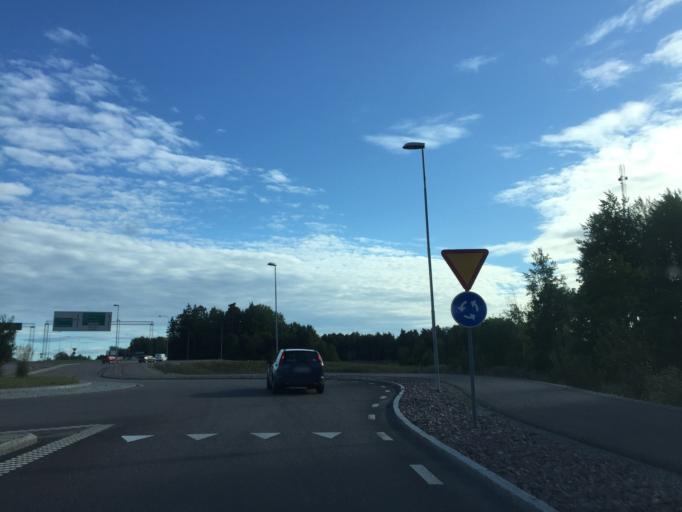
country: SE
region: Vaestmanland
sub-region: Vasteras
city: Vasteras
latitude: 59.6076
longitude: 16.4496
